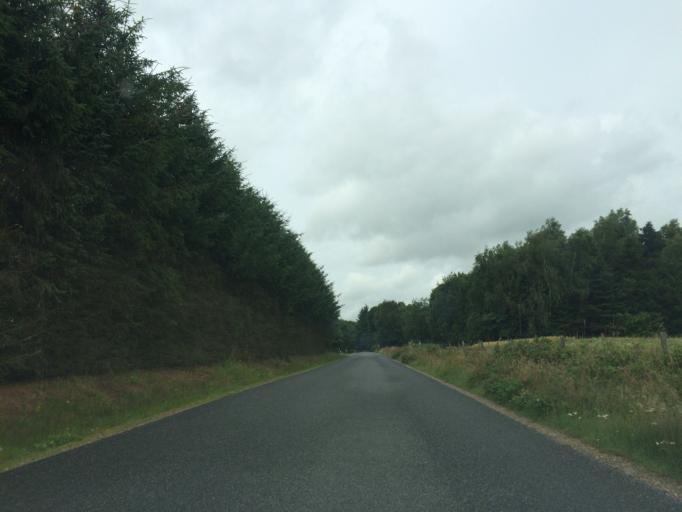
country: DK
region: Central Jutland
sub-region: Silkeborg Kommune
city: Svejbaek
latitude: 56.2406
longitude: 9.6755
